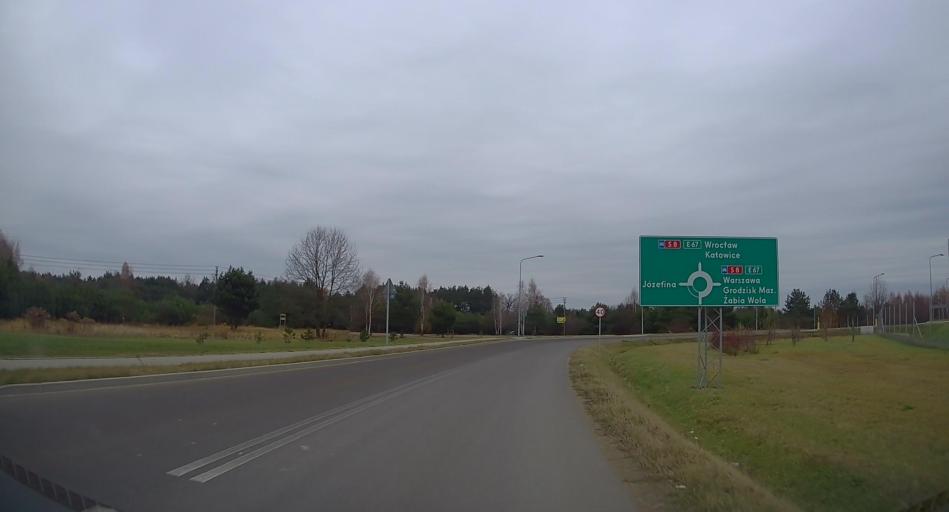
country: PL
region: Lodz Voivodeship
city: Zabia Wola
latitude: 52.0262
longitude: 20.6588
